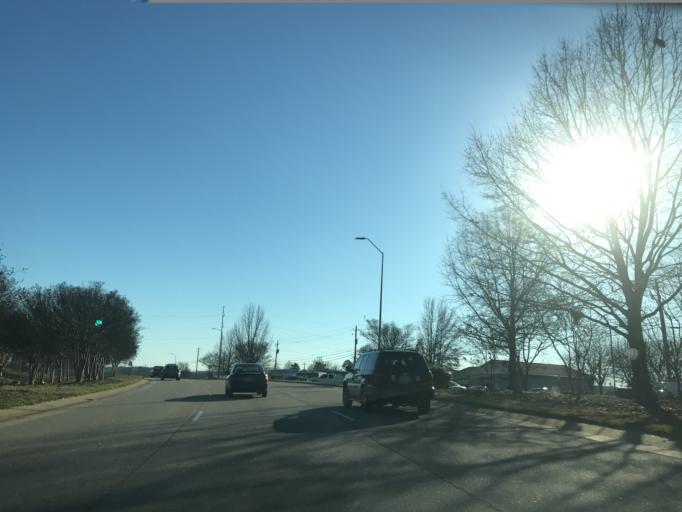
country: US
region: North Carolina
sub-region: Wake County
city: Raleigh
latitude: 35.7651
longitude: -78.6488
